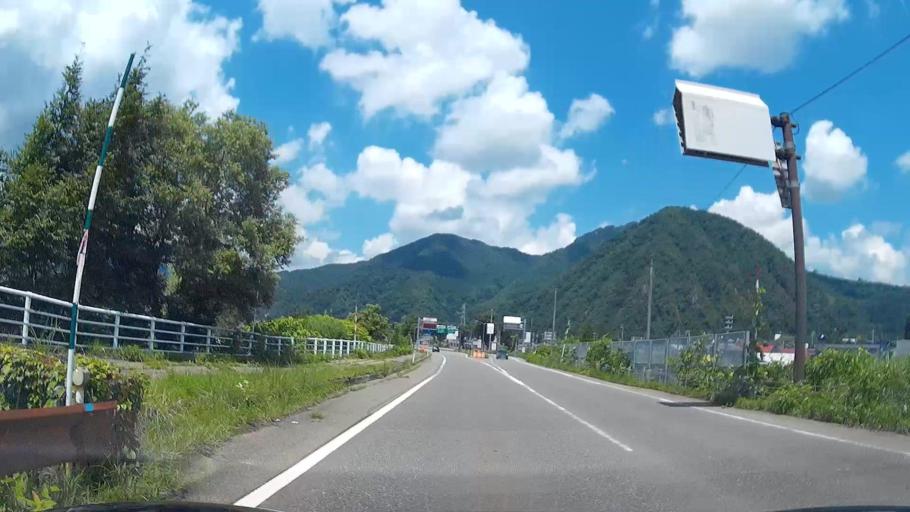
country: JP
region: Niigata
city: Shiozawa
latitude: 36.9282
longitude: 138.8238
